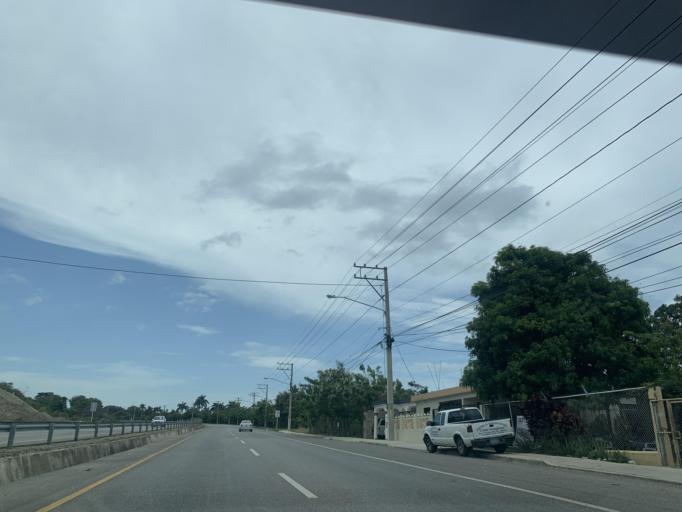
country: DO
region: Puerto Plata
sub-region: Puerto Plata
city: Puerto Plata
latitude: 19.8271
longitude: -70.7488
